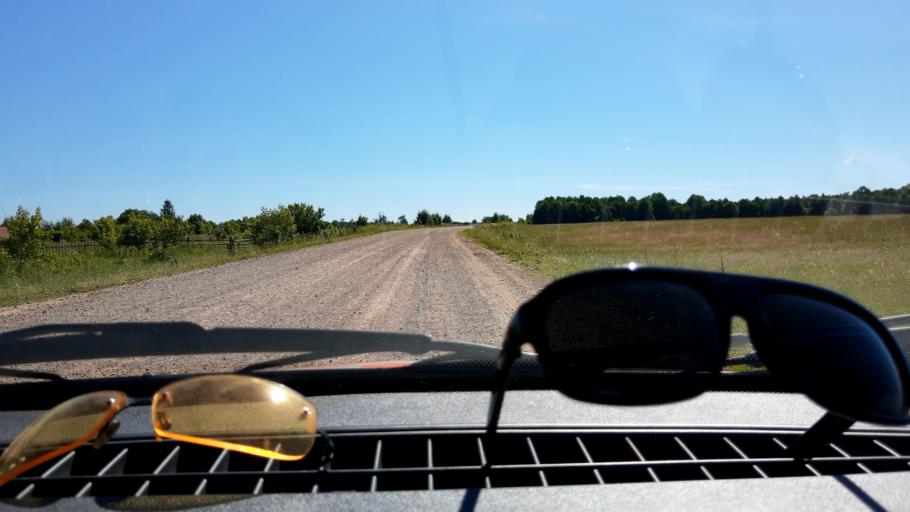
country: RU
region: Bashkortostan
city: Ulu-Telyak
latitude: 54.7957
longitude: 57.0094
